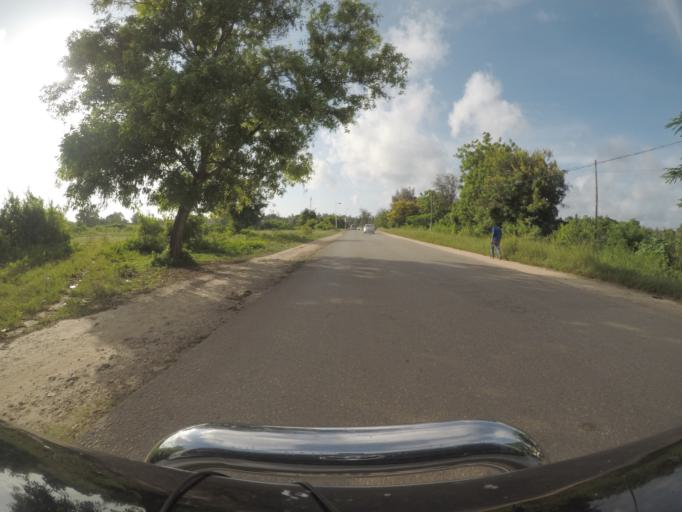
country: TZ
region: Zanzibar Central/South
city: Koani
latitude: -6.1966
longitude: 39.3059
